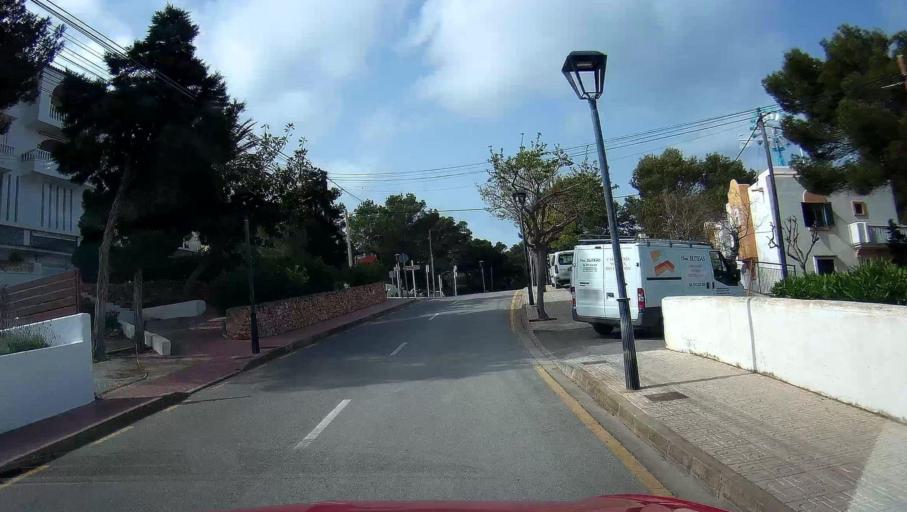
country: ES
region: Balearic Islands
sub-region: Illes Balears
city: Sant Joan de Labritja
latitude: 39.1128
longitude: 1.5179
